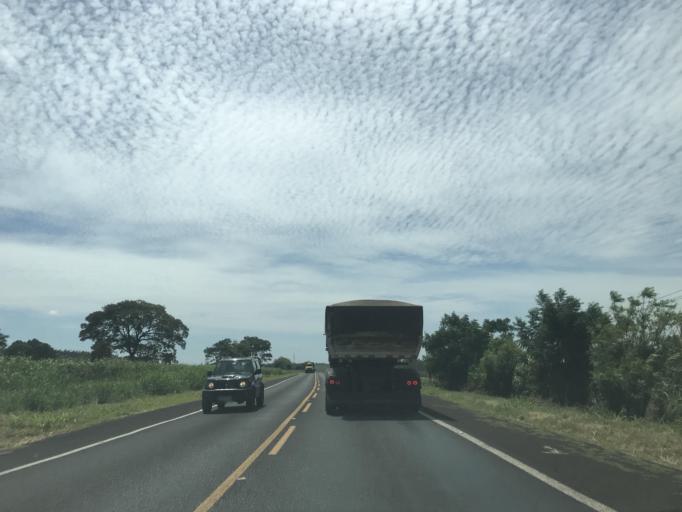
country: BR
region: Parana
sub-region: Paranavai
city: Paranavai
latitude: -23.0153
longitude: -52.5271
